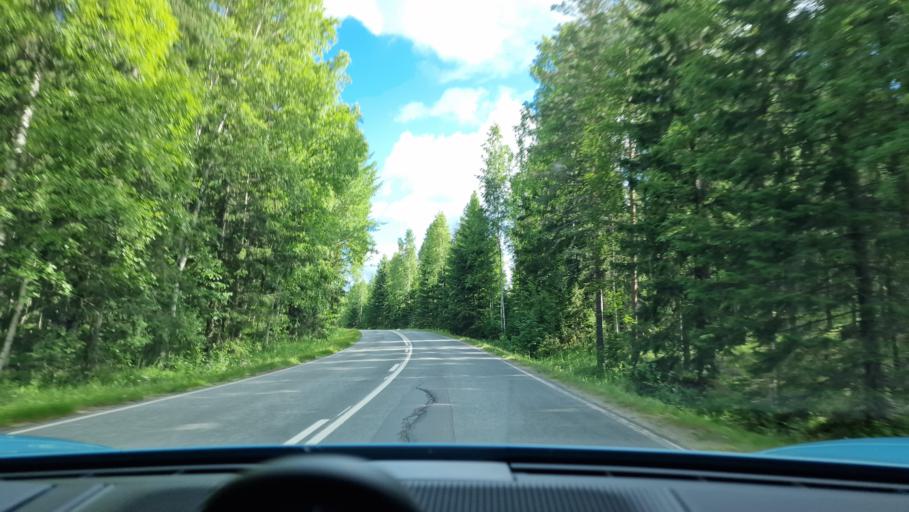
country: FI
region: Pirkanmaa
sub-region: Tampere
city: Paelkaene
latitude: 61.2619
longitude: 24.2360
